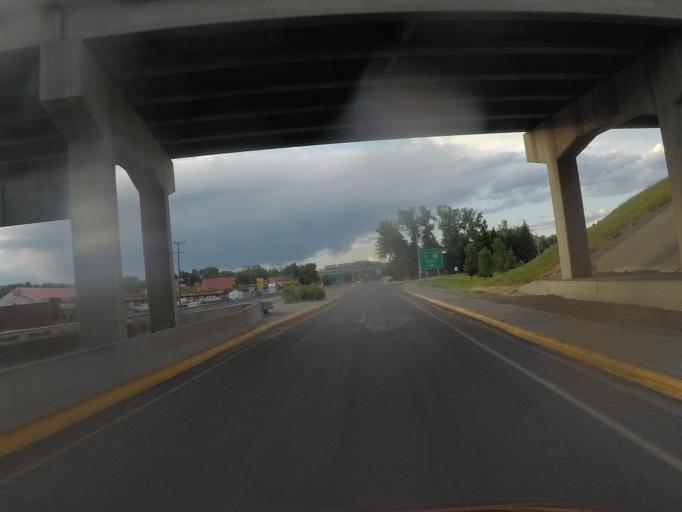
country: US
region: Montana
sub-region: Park County
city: Livingston
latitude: 45.6444
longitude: -110.5735
